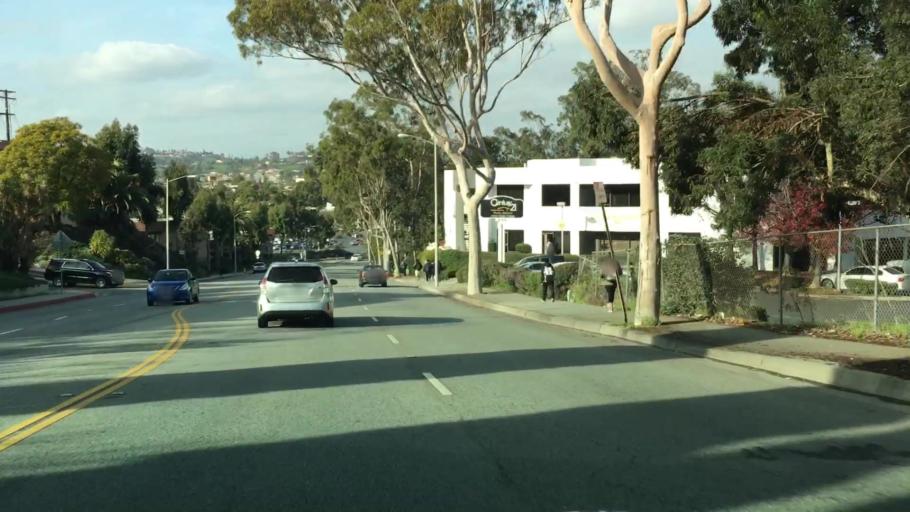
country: US
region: California
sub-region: Los Angeles County
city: Montebello
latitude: 34.0291
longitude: -118.1244
